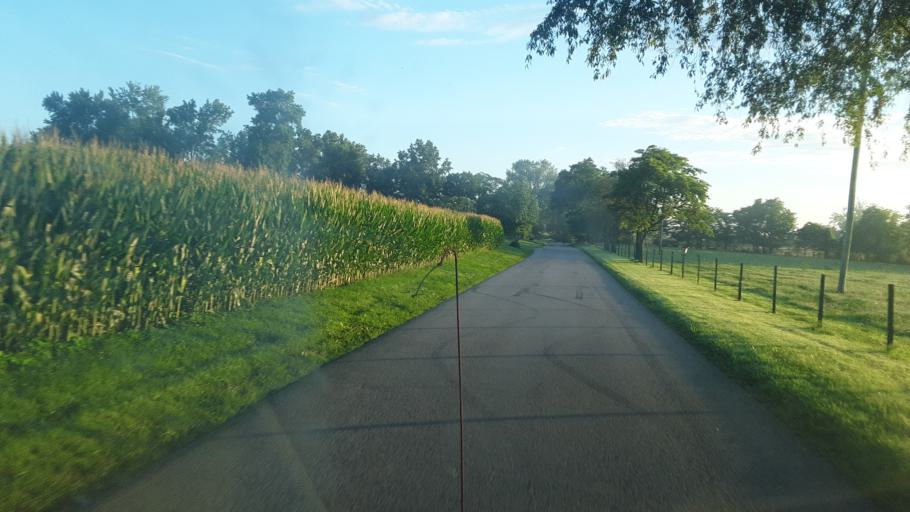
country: US
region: Kentucky
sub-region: Todd County
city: Guthrie
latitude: 36.6789
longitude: -87.1689
